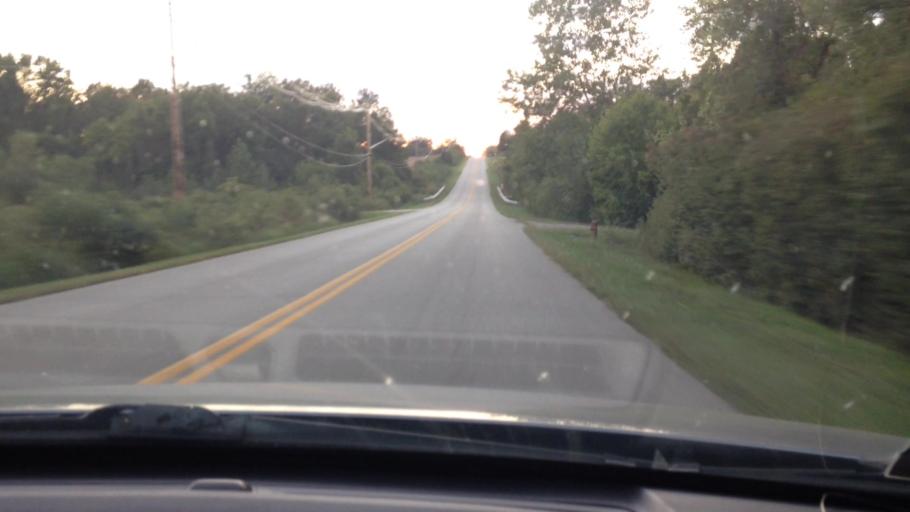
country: US
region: Kansas
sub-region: Leavenworth County
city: Lansing
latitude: 39.1868
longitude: -94.8530
